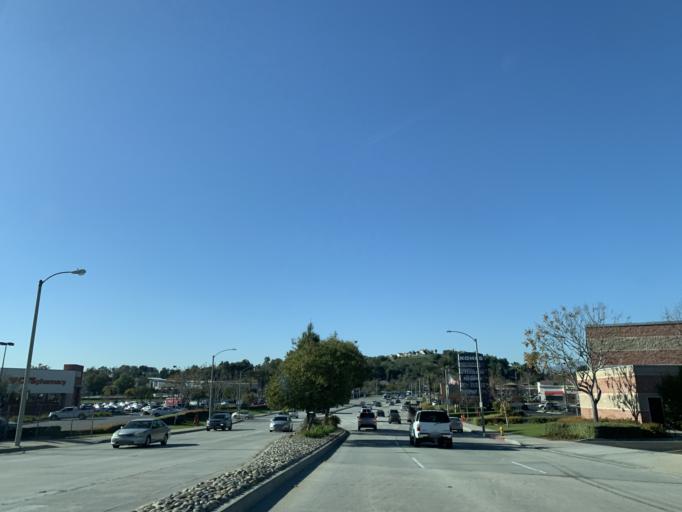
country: US
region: California
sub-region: Los Angeles County
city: Diamond Bar
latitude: 34.0259
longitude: -117.8335
